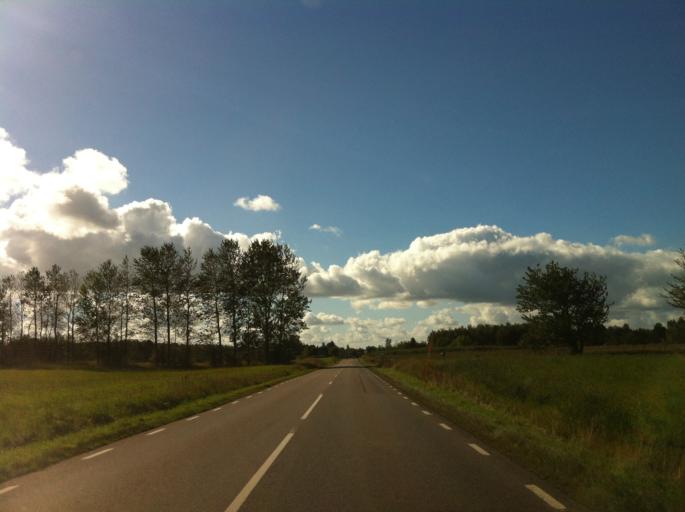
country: SE
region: Skane
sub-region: Sjobo Kommun
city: Sjoebo
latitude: 55.6343
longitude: 13.7419
